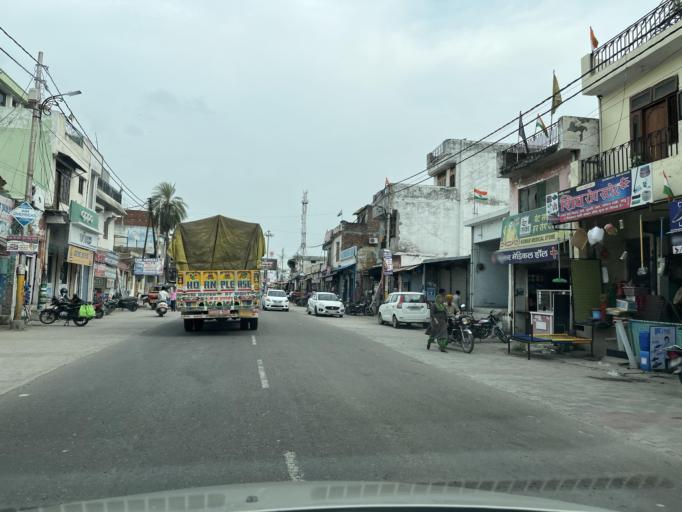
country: IN
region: Uttar Pradesh
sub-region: Rampur
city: Bilaspur
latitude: 29.0417
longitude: 79.2489
